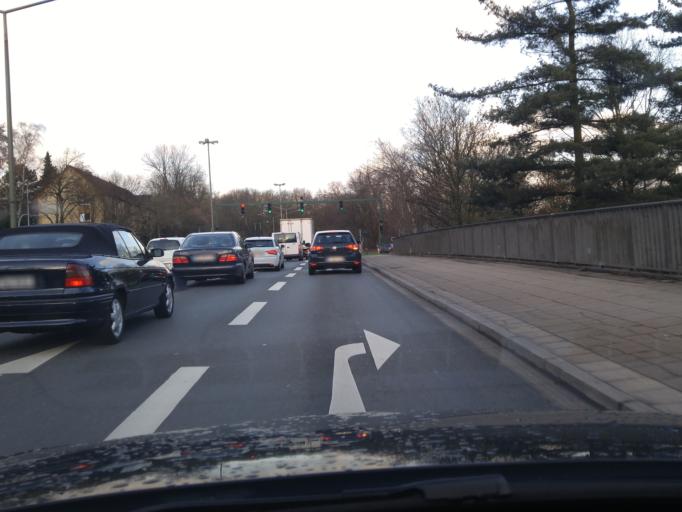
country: DE
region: North Rhine-Westphalia
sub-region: Regierungsbezirk Dusseldorf
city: Essen
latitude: 51.4306
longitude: 7.0555
